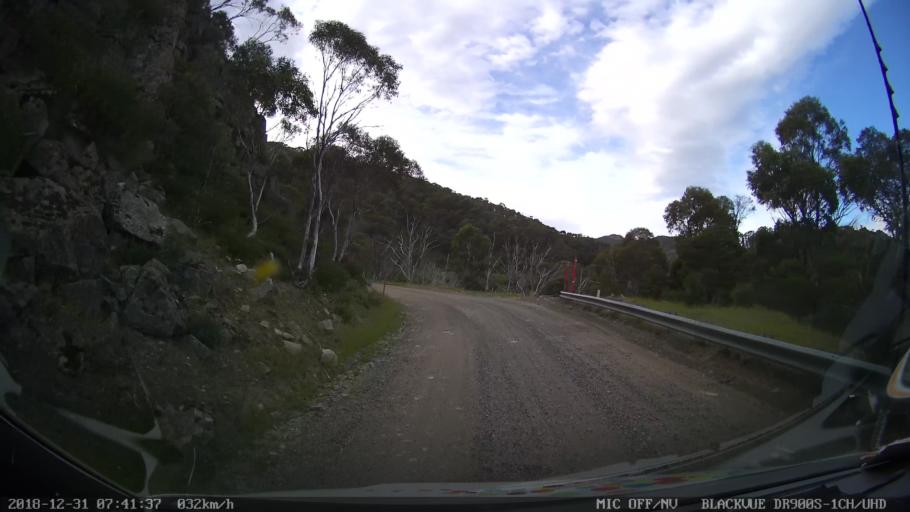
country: AU
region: New South Wales
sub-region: Snowy River
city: Jindabyne
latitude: -36.3538
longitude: 148.4114
